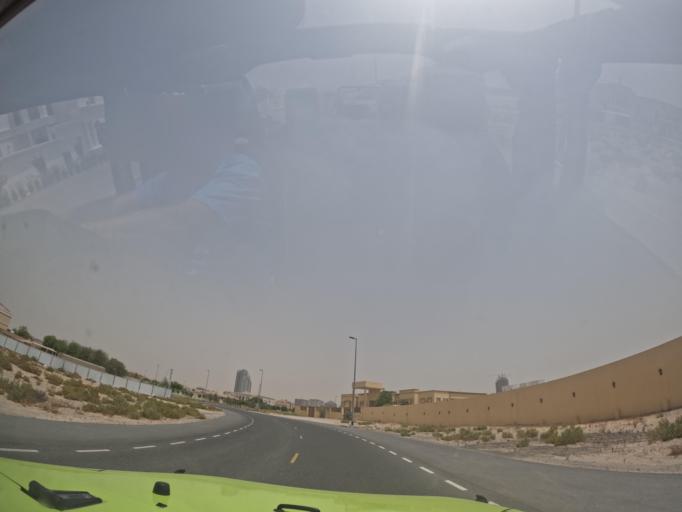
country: AE
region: Dubai
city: Dubai
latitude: 25.1261
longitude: 55.3653
